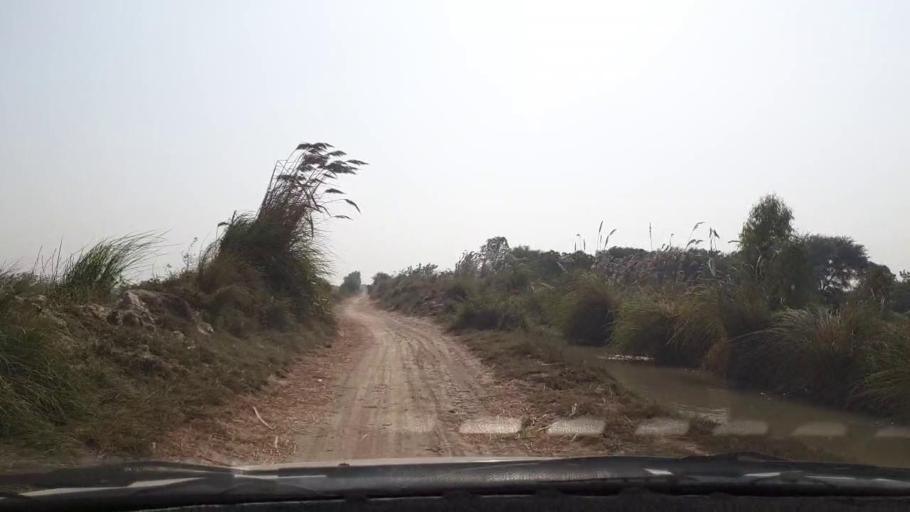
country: PK
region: Sindh
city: Tando Muhammad Khan
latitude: 25.0866
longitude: 68.3587
